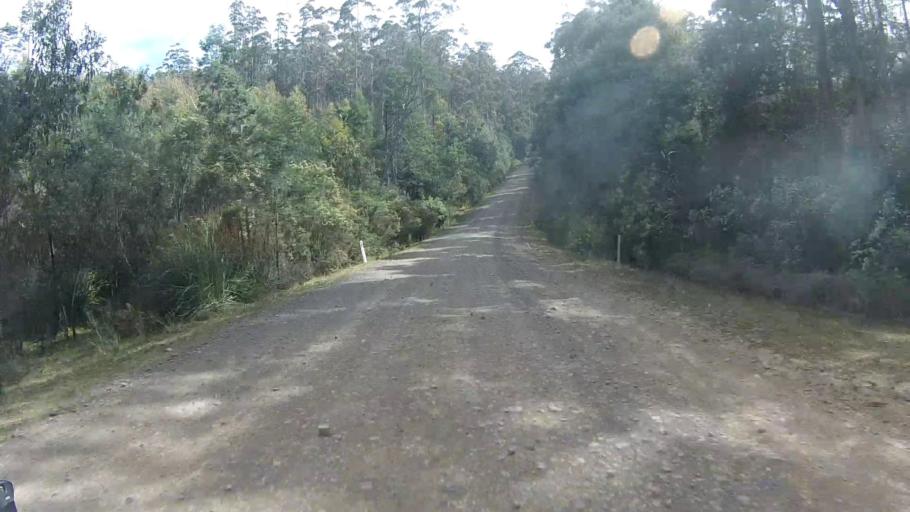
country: AU
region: Tasmania
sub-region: Sorell
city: Sorell
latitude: -42.7409
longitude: 147.8289
